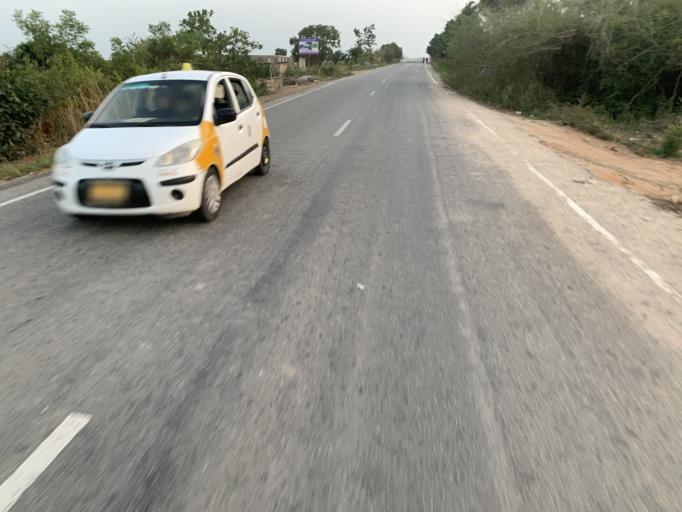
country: GH
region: Central
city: Winneba
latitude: 5.3717
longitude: -0.6072
